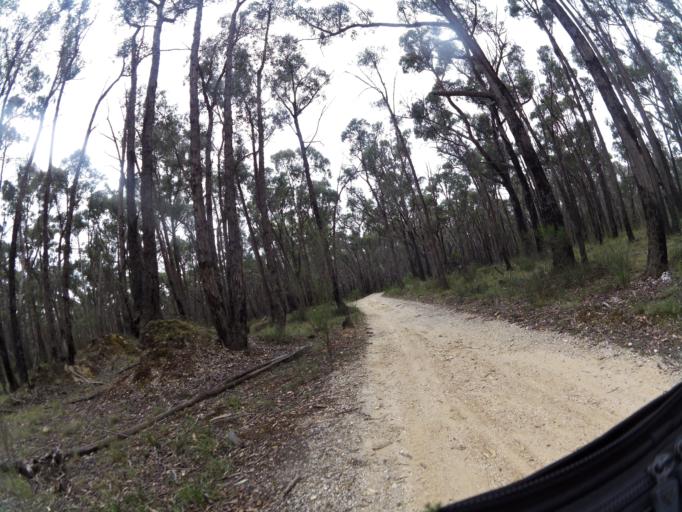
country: AU
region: Victoria
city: Brown Hill
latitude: -37.4437
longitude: 143.9093
